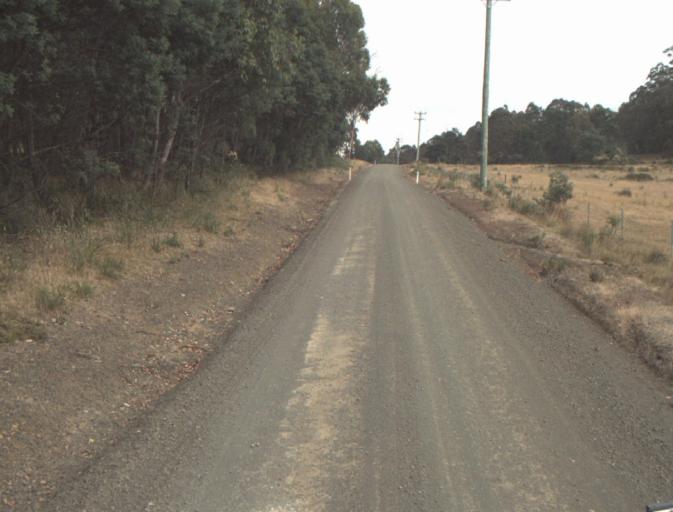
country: AU
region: Tasmania
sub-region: Northern Midlands
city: Evandale
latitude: -41.5182
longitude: 147.4205
